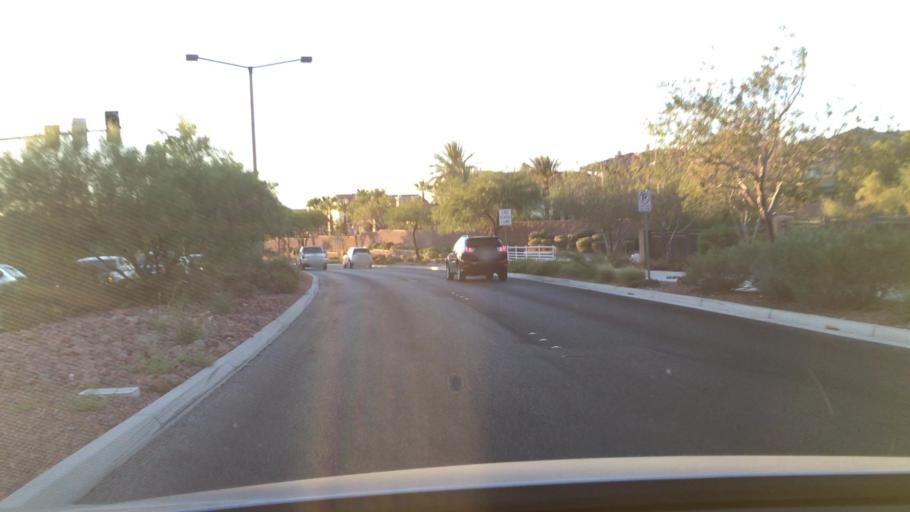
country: US
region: Nevada
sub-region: Clark County
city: Summerlin South
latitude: 36.1565
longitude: -115.3512
